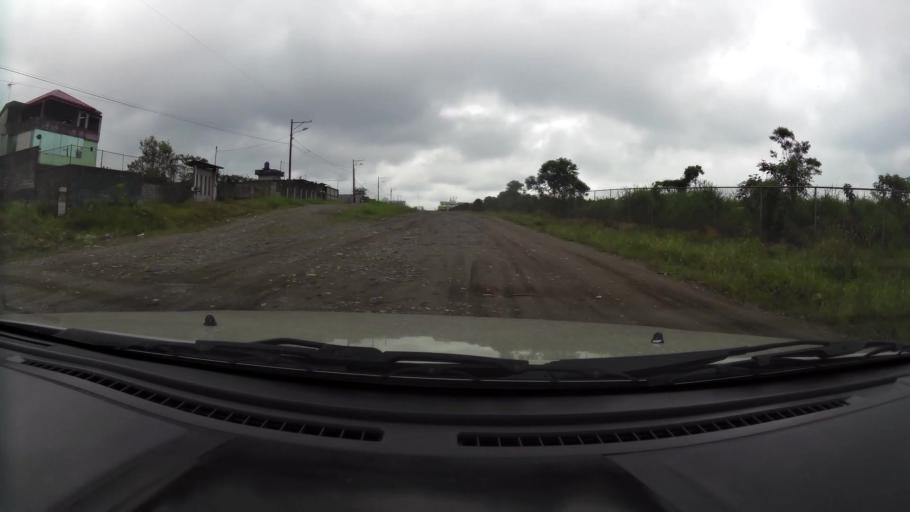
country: EC
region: Santo Domingo de los Tsachilas
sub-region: Canton Santo Domingo de los Colorados
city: Santo Domingo de los Colorados
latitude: -0.2429
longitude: -79.1604
